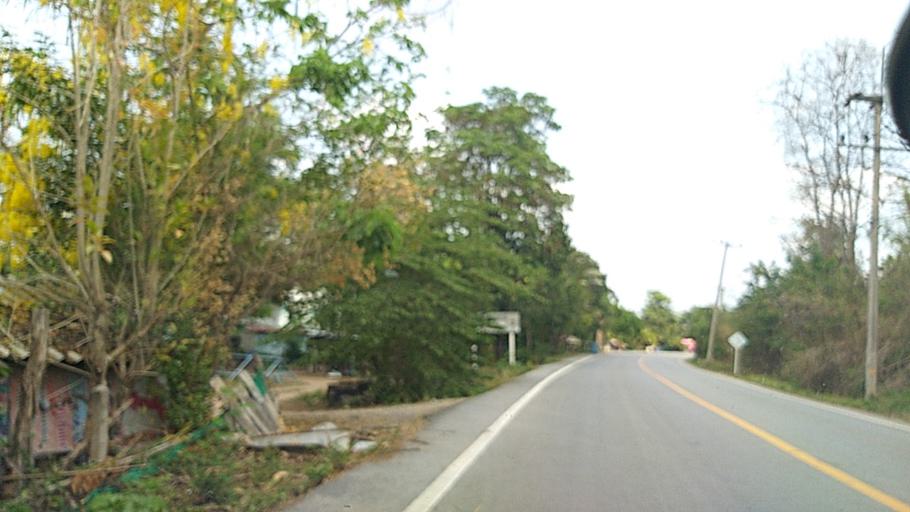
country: TH
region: Sara Buri
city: Saraburi
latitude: 14.4568
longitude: 100.9479
